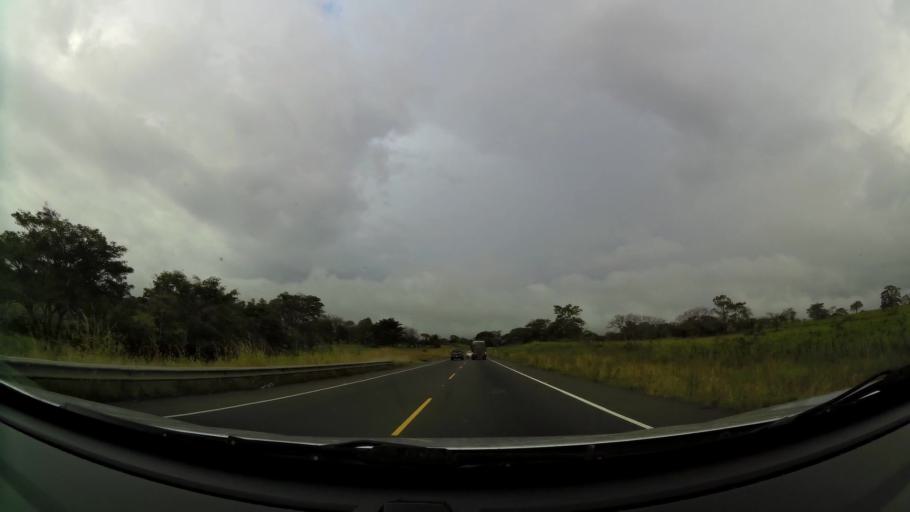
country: CR
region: Alajuela
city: Carrillos
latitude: 9.9648
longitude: -84.2949
